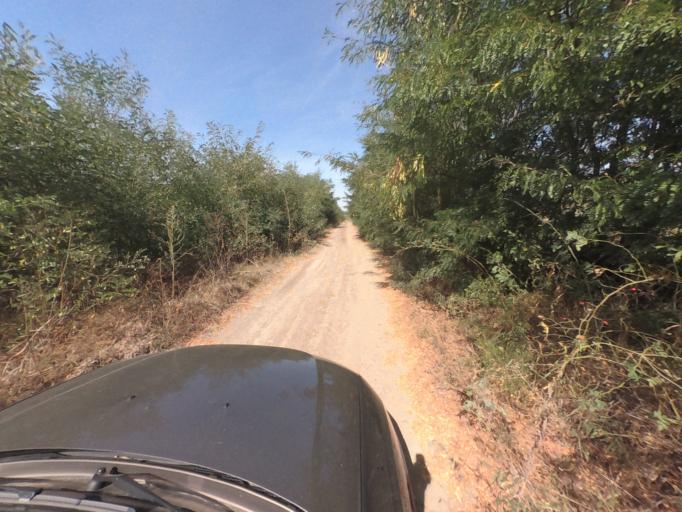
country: RO
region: Vaslui
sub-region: Comuna Costesti
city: Costesti
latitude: 46.5212
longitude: 27.7396
